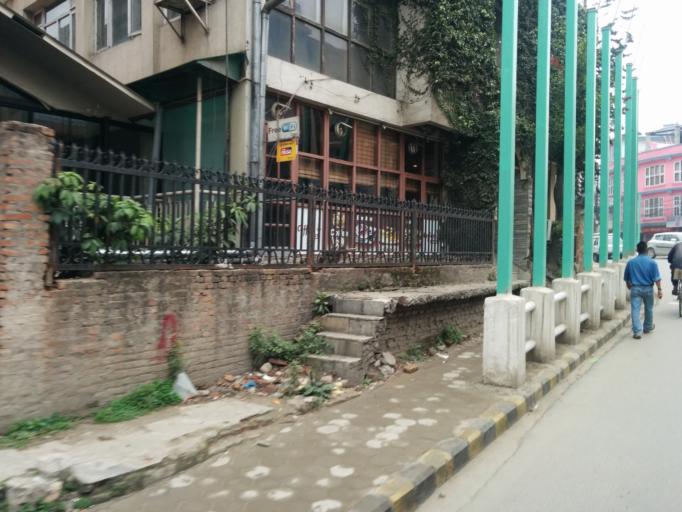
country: NP
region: Central Region
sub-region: Bagmati Zone
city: Kathmandu
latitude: 27.7099
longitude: 85.3221
